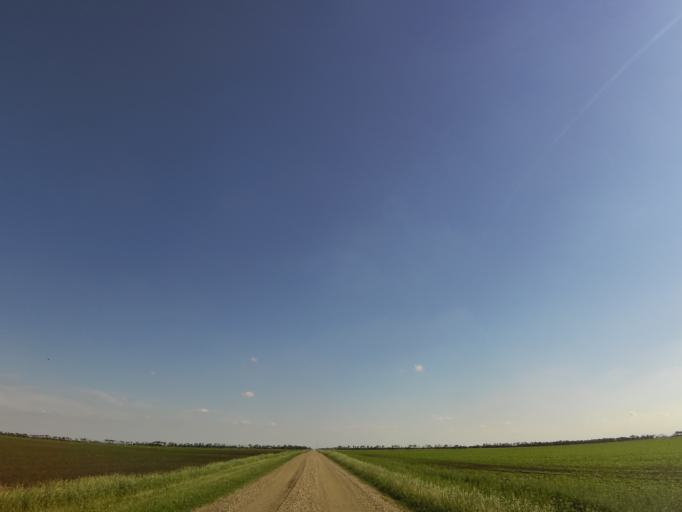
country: US
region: North Dakota
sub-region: Walsh County
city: Grafton
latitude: 48.3427
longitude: -97.2329
